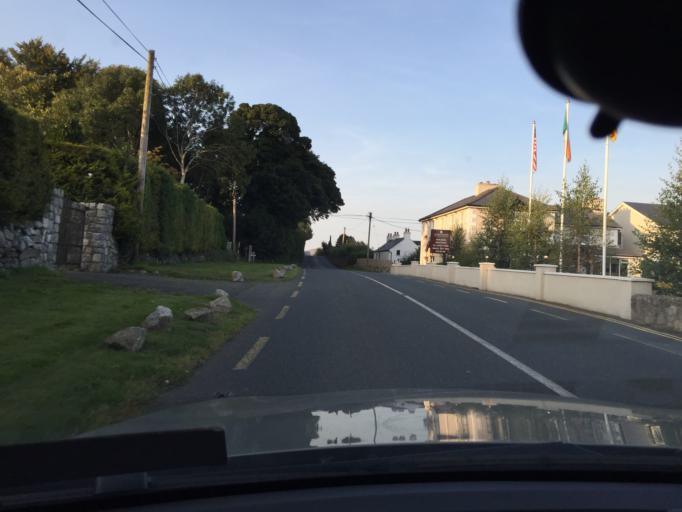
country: IE
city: Newtownmountkennedy
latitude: 53.1044
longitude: -6.1953
